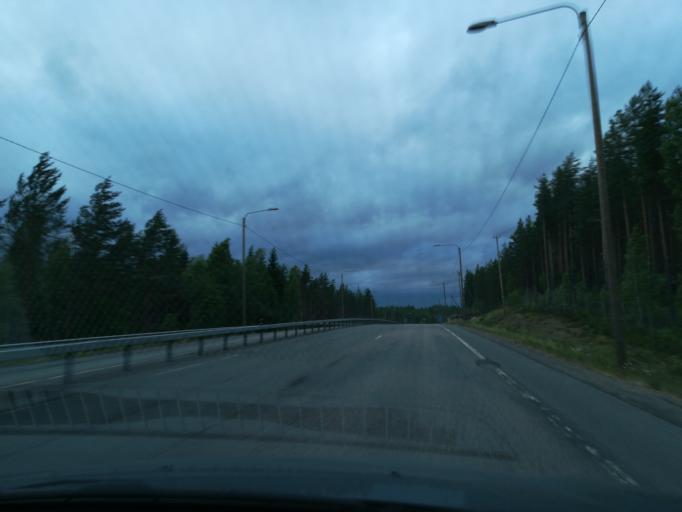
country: FI
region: Southern Savonia
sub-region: Mikkeli
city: Ristiina
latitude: 61.4080
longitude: 27.3459
